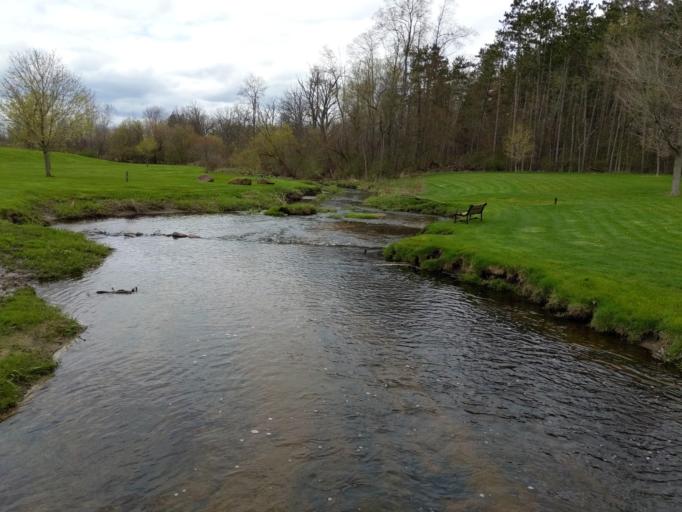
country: US
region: Michigan
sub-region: Eaton County
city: Eaton Rapids
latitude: 42.5683
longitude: -84.5873
